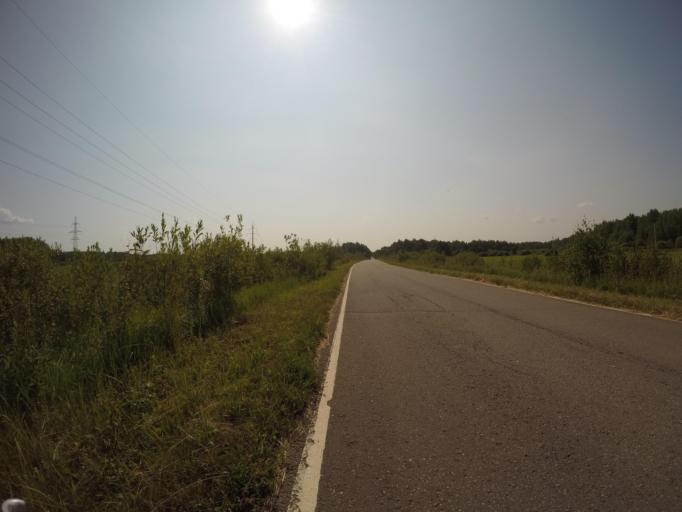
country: RU
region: Moskovskaya
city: Rechitsy
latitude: 55.6250
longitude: 38.5220
